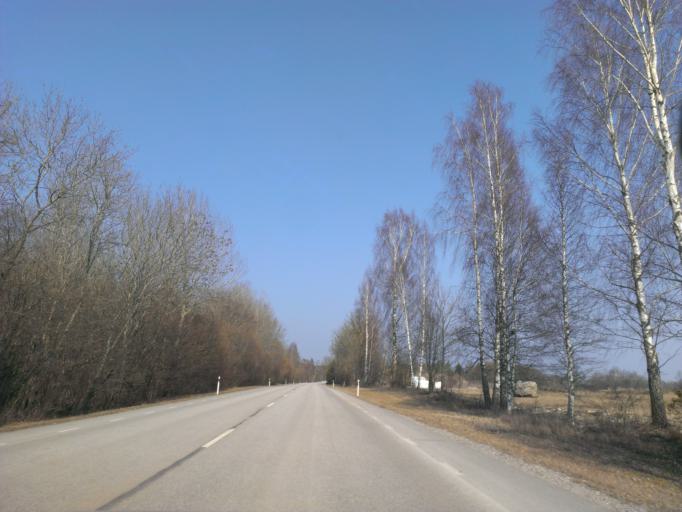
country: EE
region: Saare
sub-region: Orissaare vald
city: Orissaare
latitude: 58.5377
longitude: 23.0491
